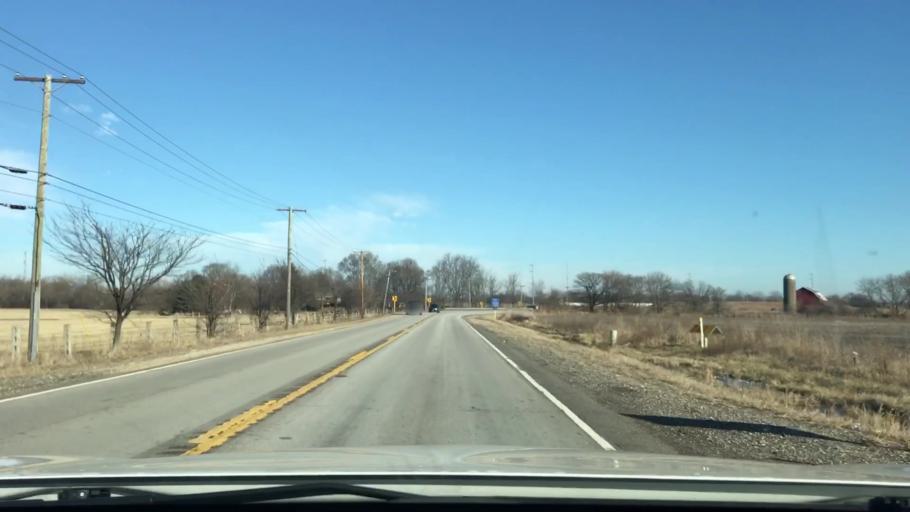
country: US
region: Illinois
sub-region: Kane County
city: Gilberts
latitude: 42.0991
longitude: -88.3971
